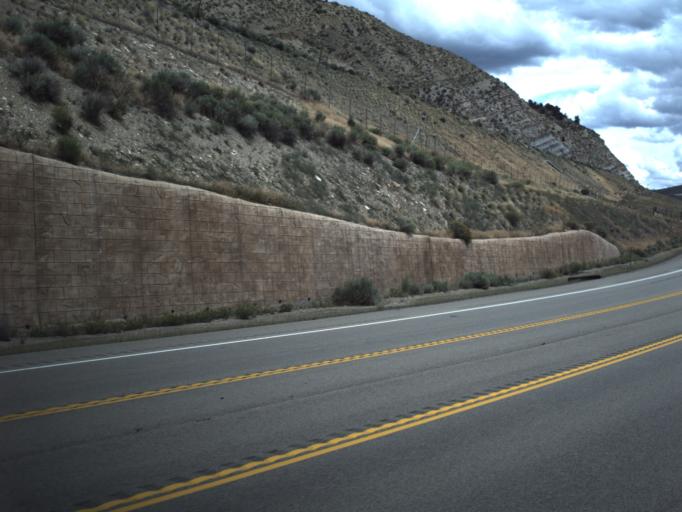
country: US
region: Utah
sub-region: Sanpete County
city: Fairview
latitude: 39.9299
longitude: -111.1969
